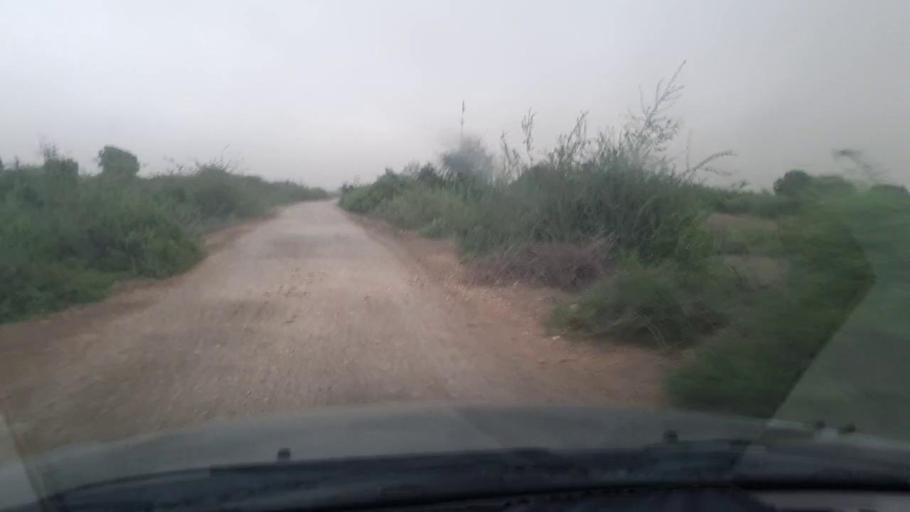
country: PK
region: Sindh
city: Digri
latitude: 25.0044
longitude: 69.0804
